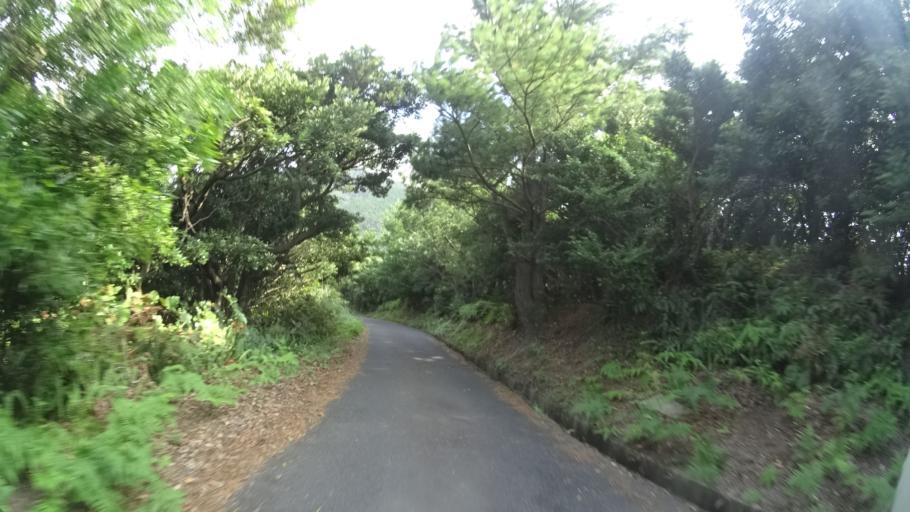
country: JP
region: Kagoshima
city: Nishinoomote
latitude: 30.3911
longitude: 130.3833
